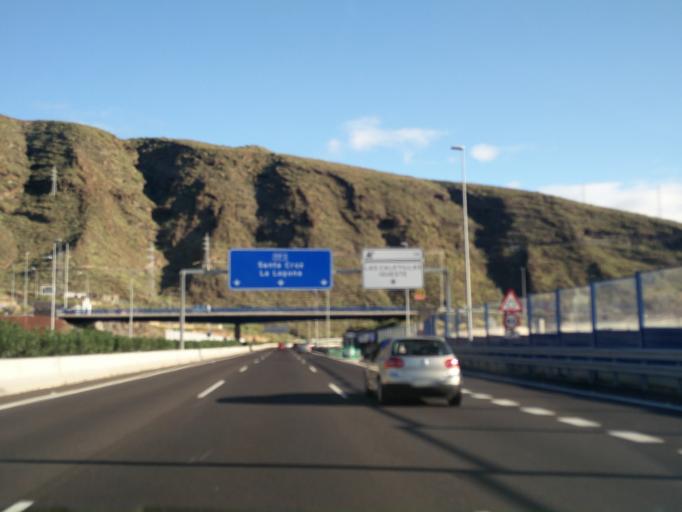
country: ES
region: Canary Islands
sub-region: Provincia de Santa Cruz de Tenerife
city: Candelaria
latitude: 28.3802
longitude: -16.3637
